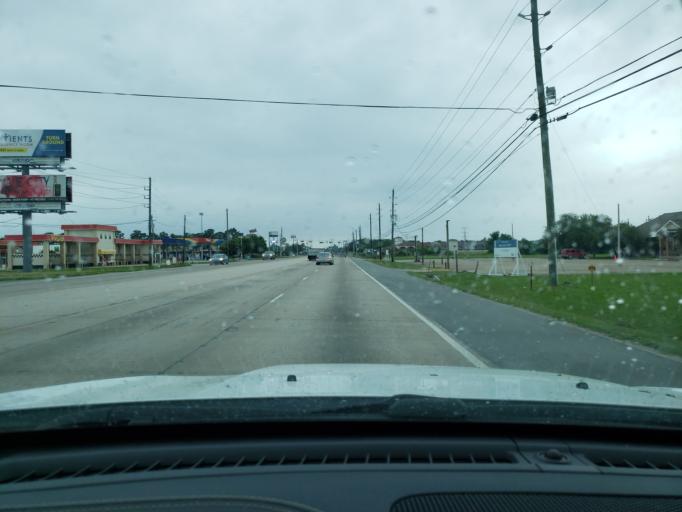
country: US
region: Texas
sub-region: Chambers County
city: Mont Belvieu
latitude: 29.8117
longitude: -94.9021
